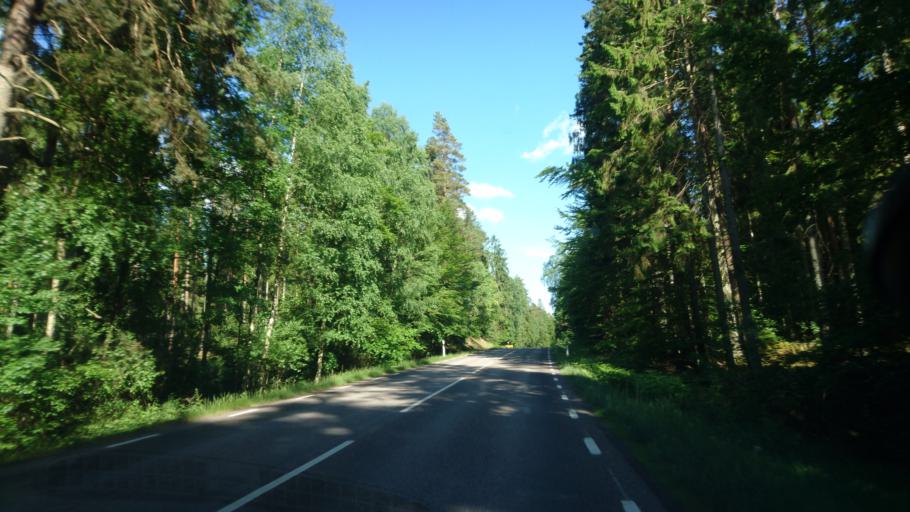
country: SE
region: Skane
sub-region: Osby Kommun
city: Lonsboda
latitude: 56.3905
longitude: 14.3612
